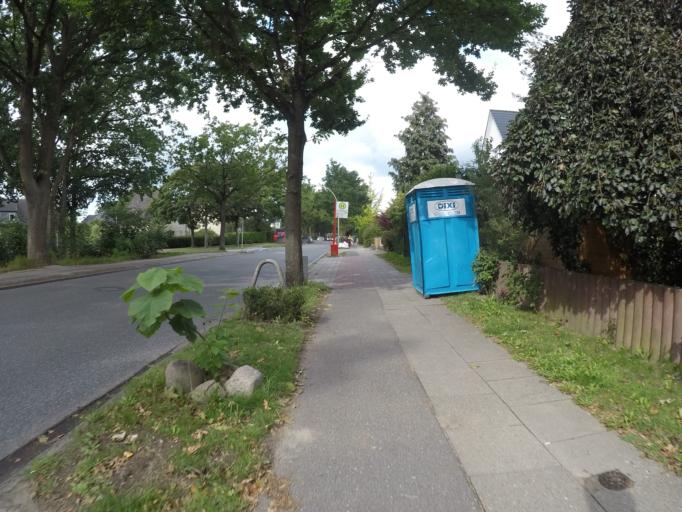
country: DE
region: Hamburg
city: Eidelstedt
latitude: 53.6111
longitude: 9.8957
